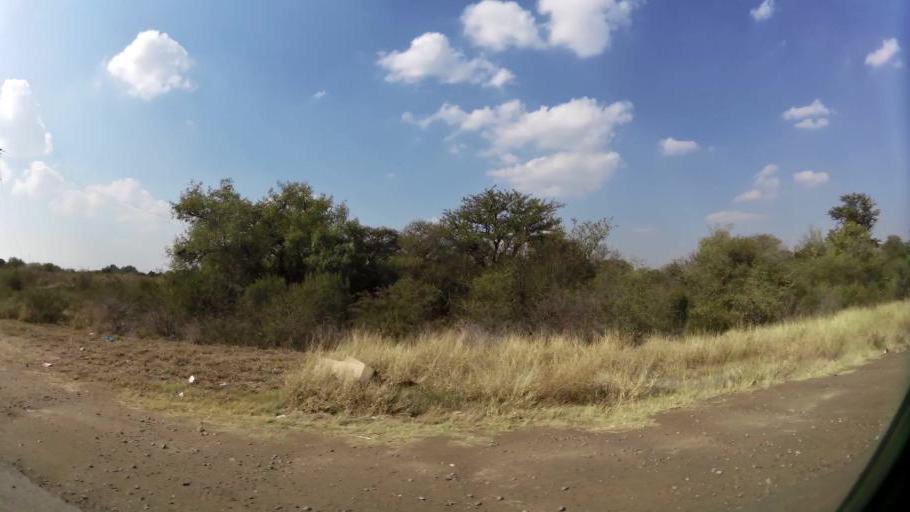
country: ZA
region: North-West
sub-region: Bojanala Platinum District Municipality
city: Mogwase
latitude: -25.4521
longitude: 27.0879
